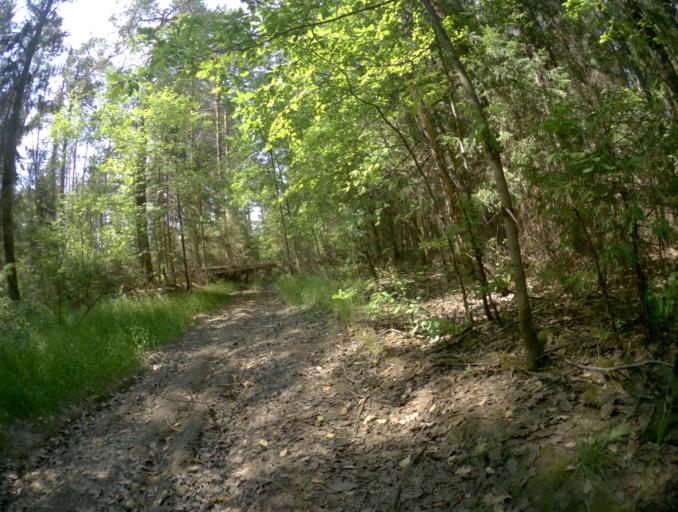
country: RU
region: Vladimir
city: Raduzhnyy
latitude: 56.0235
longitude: 40.2534
